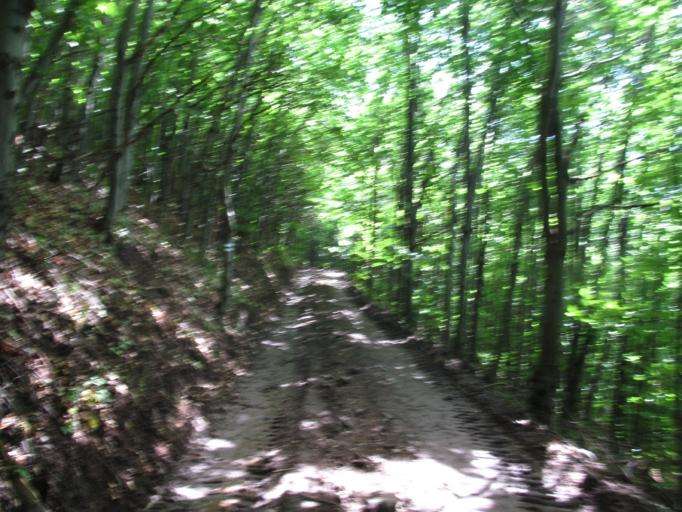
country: HU
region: Borsod-Abauj-Zemplen
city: Gonc
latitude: 48.5787
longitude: 21.4417
